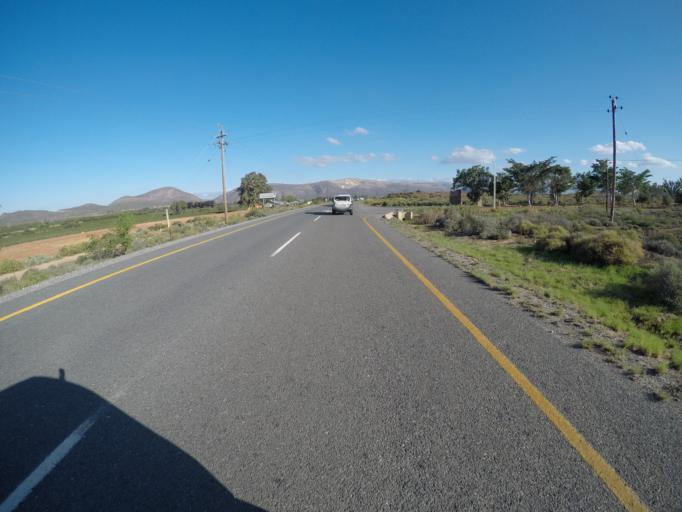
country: ZA
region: Western Cape
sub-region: Cape Winelands District Municipality
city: Ashton
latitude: -33.7931
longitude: 19.7802
